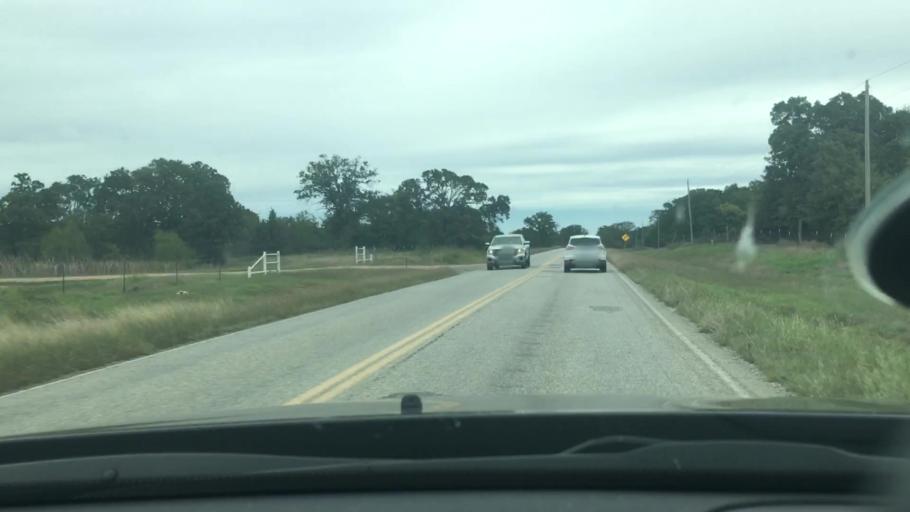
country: US
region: Oklahoma
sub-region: Johnston County
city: Tishomingo
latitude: 34.3181
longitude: -96.4247
